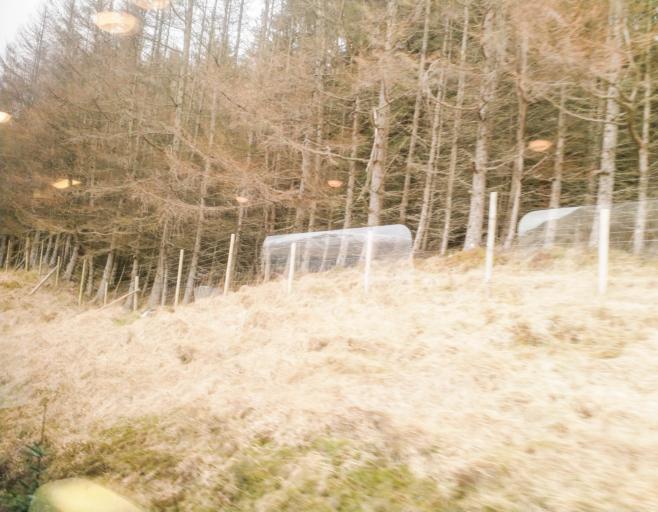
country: GB
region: Scotland
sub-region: Argyll and Bute
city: Garelochhead
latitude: 56.4370
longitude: -4.7056
